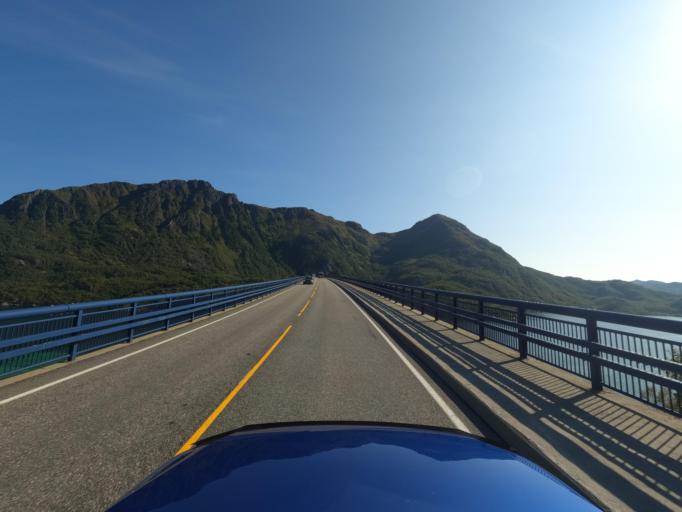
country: NO
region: Nordland
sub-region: Hadsel
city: Stokmarknes
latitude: 68.4585
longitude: 15.1864
